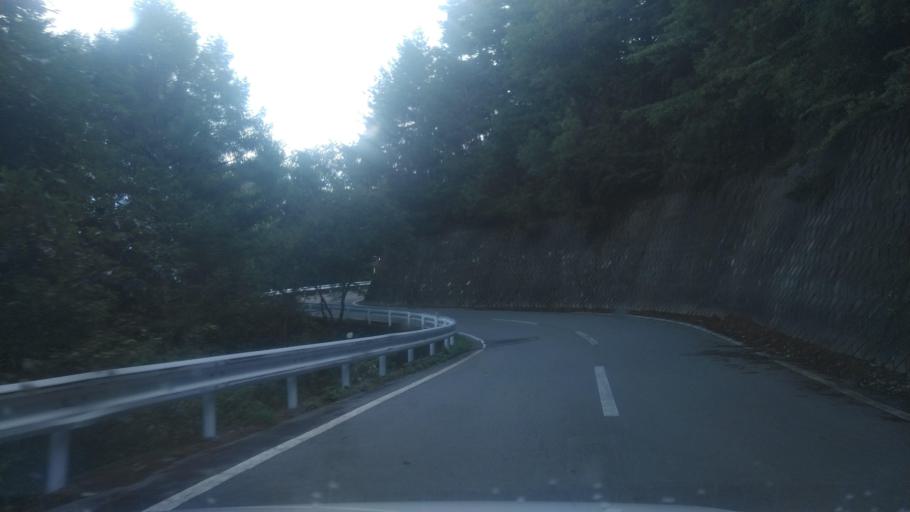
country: JP
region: Nagano
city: Ueda
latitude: 36.5083
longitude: 138.3710
